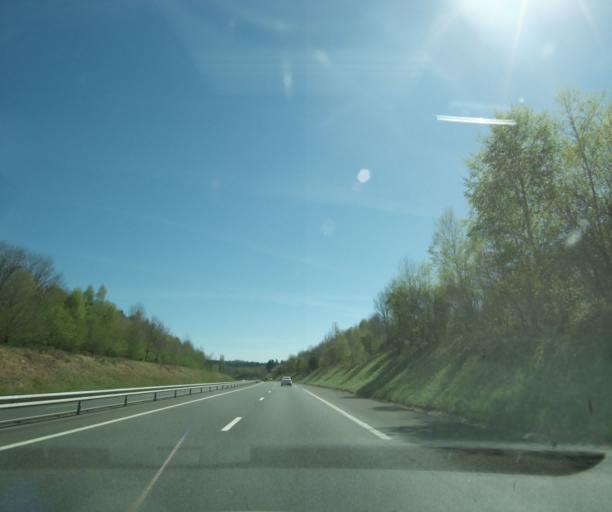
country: FR
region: Limousin
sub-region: Departement de la Correze
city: Vigeois
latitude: 45.4186
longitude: 1.5187
